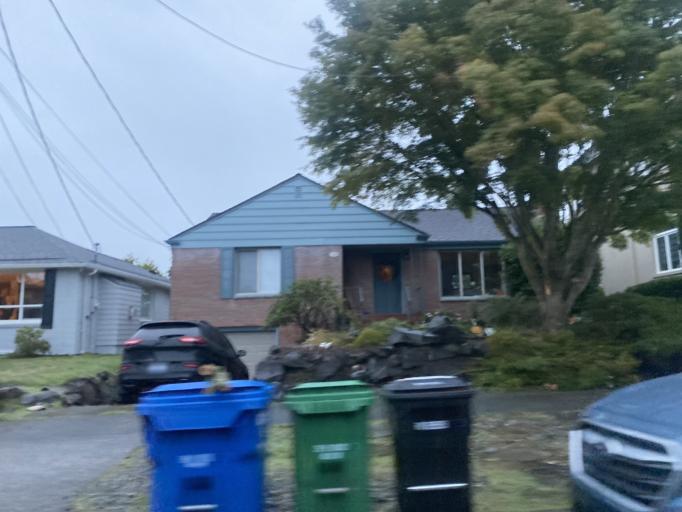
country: US
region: Washington
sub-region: King County
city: Seattle
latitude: 47.6517
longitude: -122.4058
